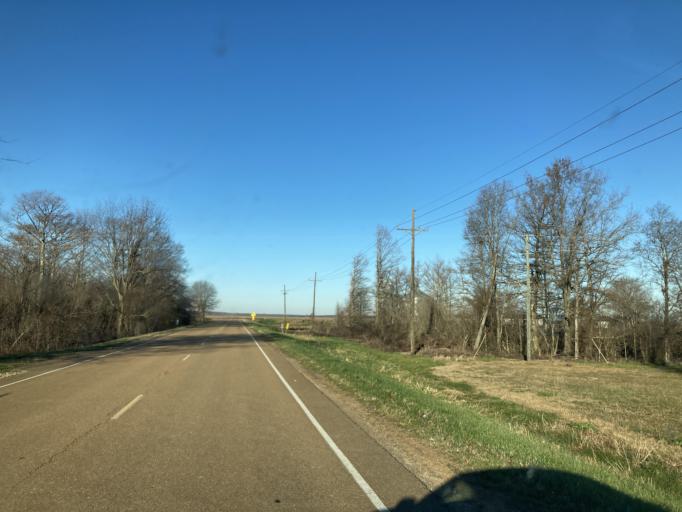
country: US
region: Mississippi
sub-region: Yazoo County
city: Yazoo City
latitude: 32.9303
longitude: -90.5975
